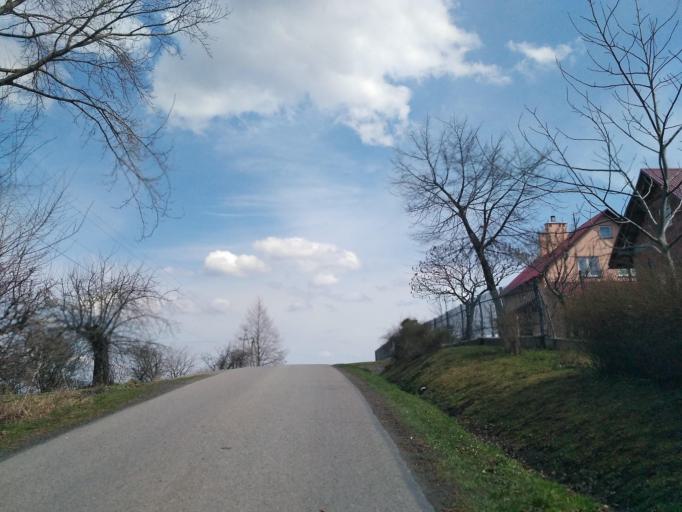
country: PL
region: Subcarpathian Voivodeship
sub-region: Powiat ropczycko-sedziszowski
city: Iwierzyce
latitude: 50.0458
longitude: 21.7244
